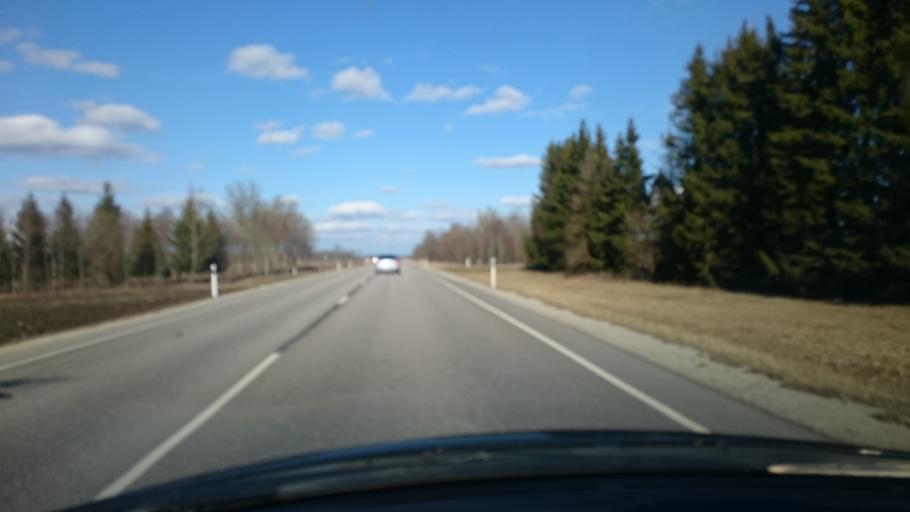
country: EE
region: Laeaene
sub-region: Lihula vald
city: Lihula
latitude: 58.7101
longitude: 23.8685
